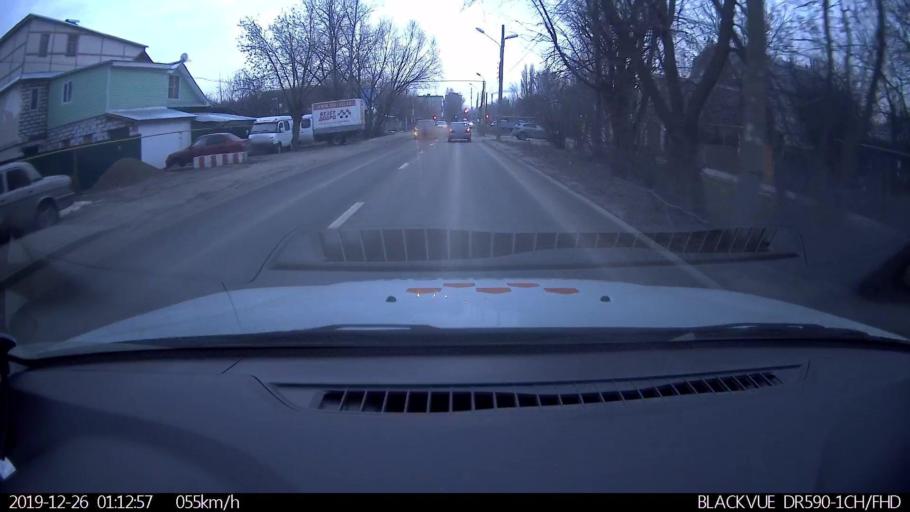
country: RU
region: Nizjnij Novgorod
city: Nizhniy Novgorod
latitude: 56.2806
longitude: 43.9130
